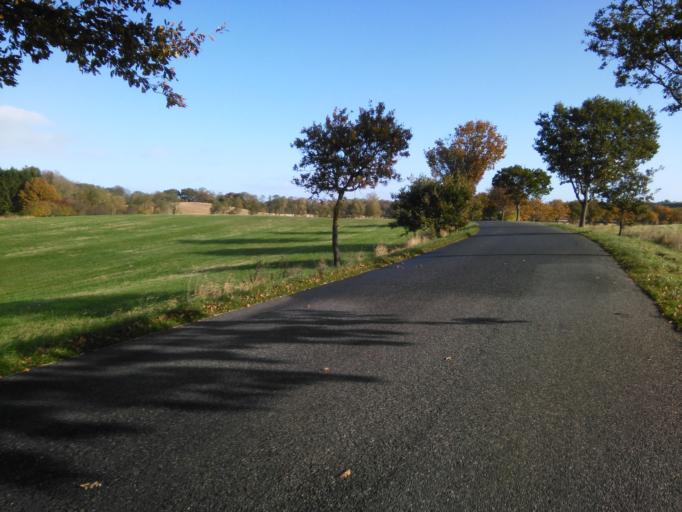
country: DK
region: Central Jutland
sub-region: Arhus Kommune
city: Beder
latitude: 56.0749
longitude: 10.2128
